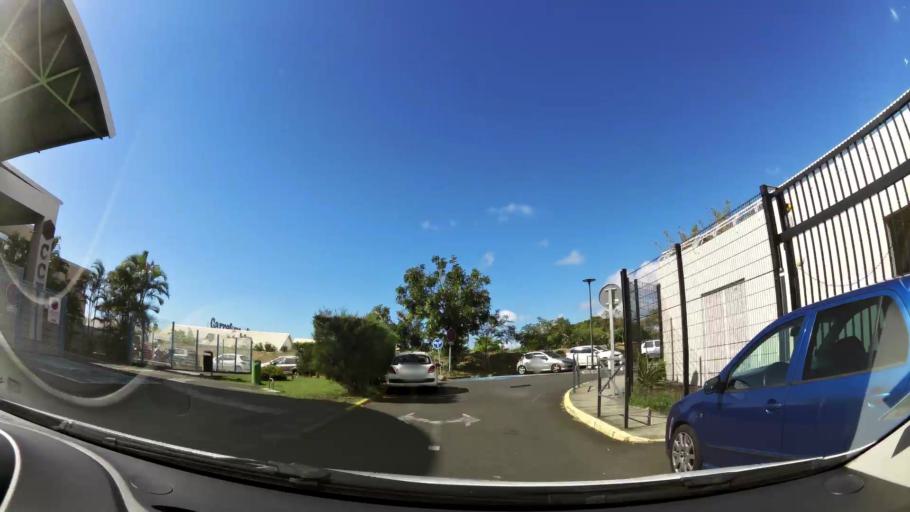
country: RE
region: Reunion
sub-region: Reunion
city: Saint-Denis
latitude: -20.8921
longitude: 55.4988
